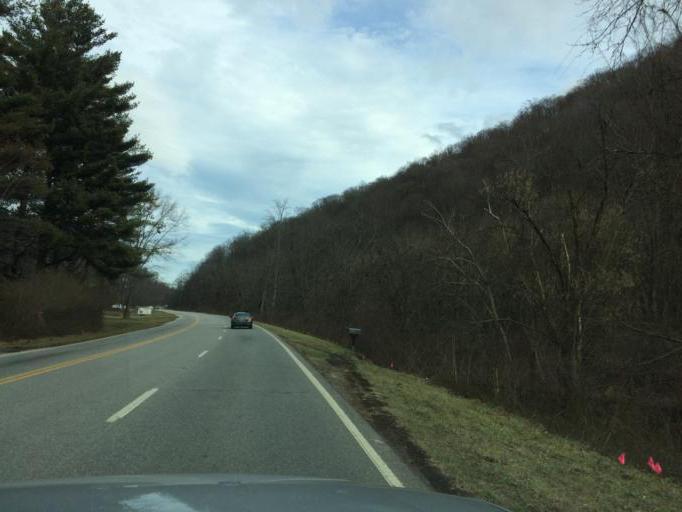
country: US
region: North Carolina
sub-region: Haywood County
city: Canton
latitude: 35.5365
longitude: -82.7906
